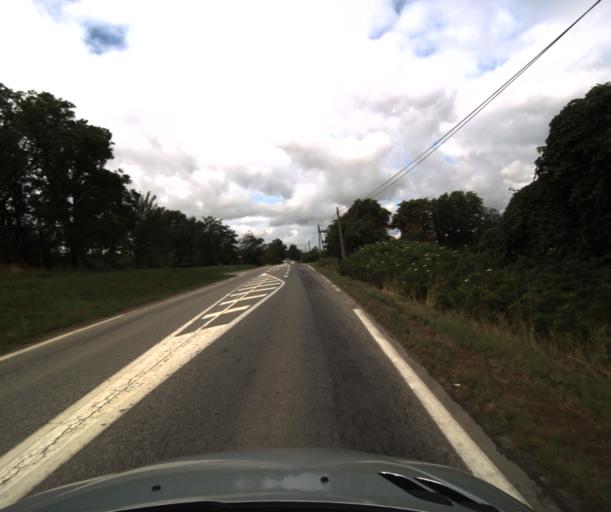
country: FR
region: Midi-Pyrenees
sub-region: Departement du Tarn-et-Garonne
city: Castelsarrasin
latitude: 44.0262
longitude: 1.0863
